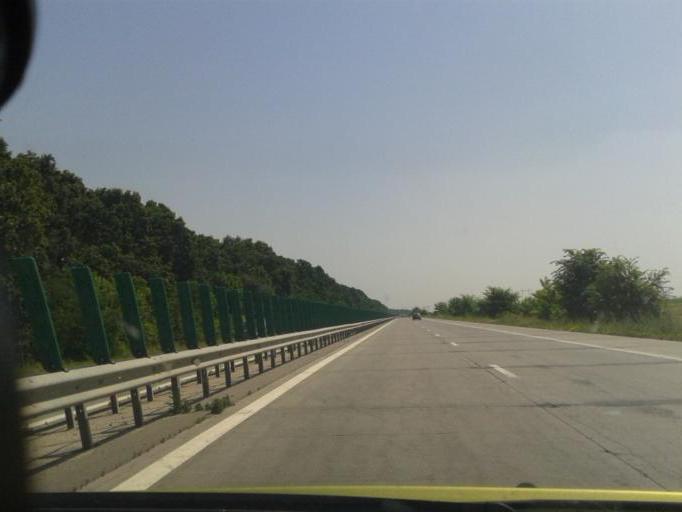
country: RO
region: Calarasi
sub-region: Comuna Belciugatele
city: Belciugatele
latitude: 44.4458
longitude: 26.4305
